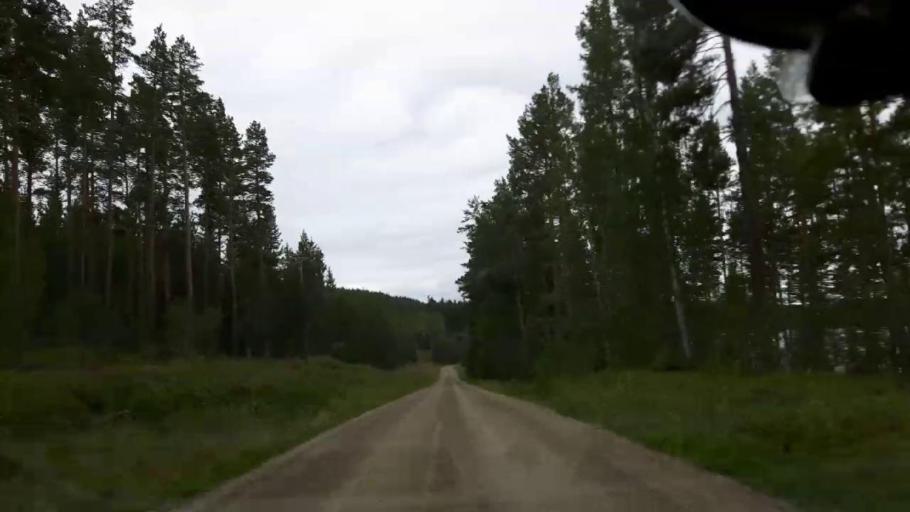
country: SE
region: Jaemtland
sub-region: Braecke Kommun
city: Braecke
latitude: 63.0073
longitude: 15.3815
